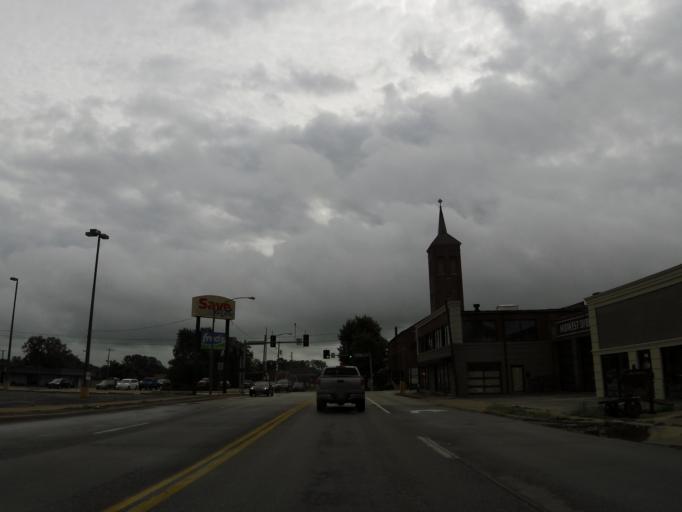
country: US
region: Missouri
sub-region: Cape Girardeau County
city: Cape Girardeau
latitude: 37.3011
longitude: -89.5283
